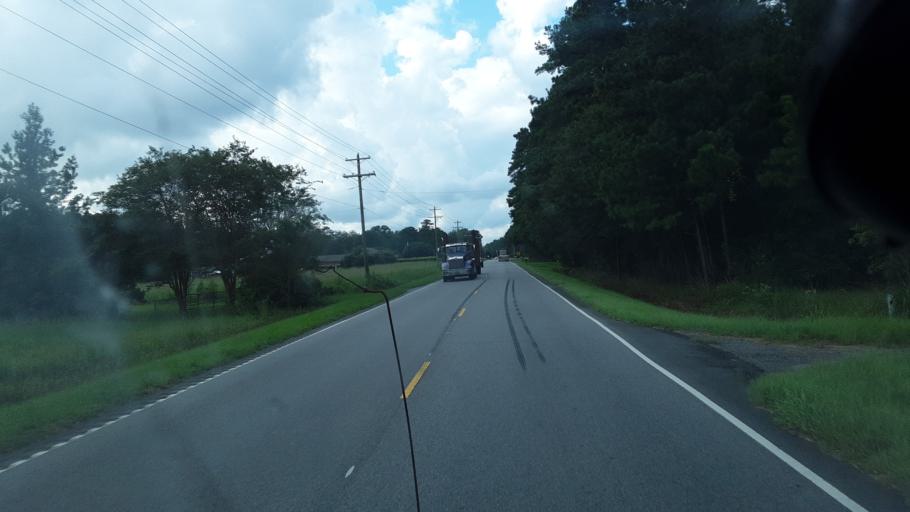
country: US
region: South Carolina
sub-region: Horry County
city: Socastee
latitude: 33.7044
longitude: -79.1053
